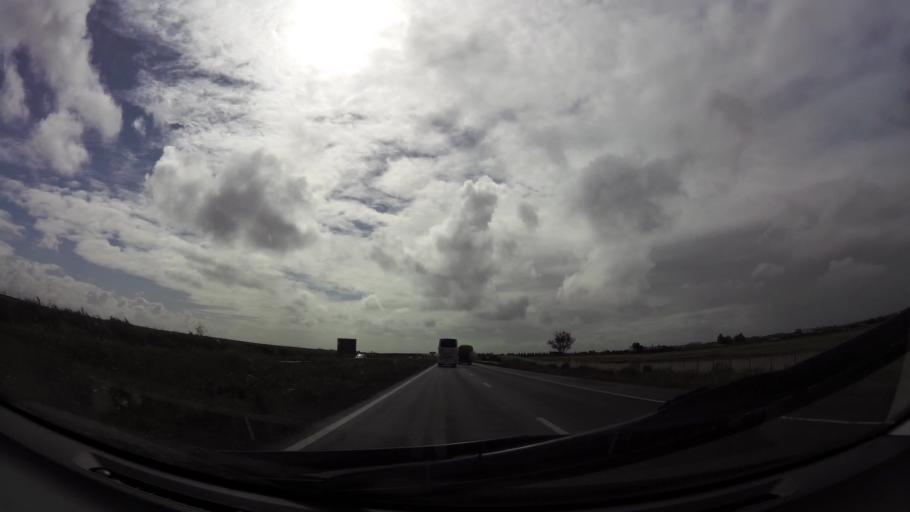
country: MA
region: Grand Casablanca
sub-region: Nouaceur
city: Dar Bouazza
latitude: 33.3536
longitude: -7.9676
